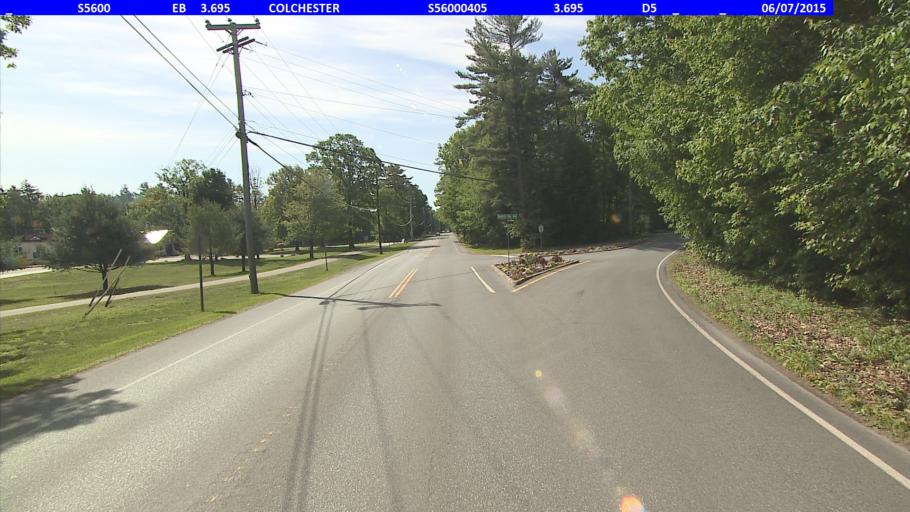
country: US
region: Vermont
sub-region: Chittenden County
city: Winooski
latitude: 44.5390
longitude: -73.2096
